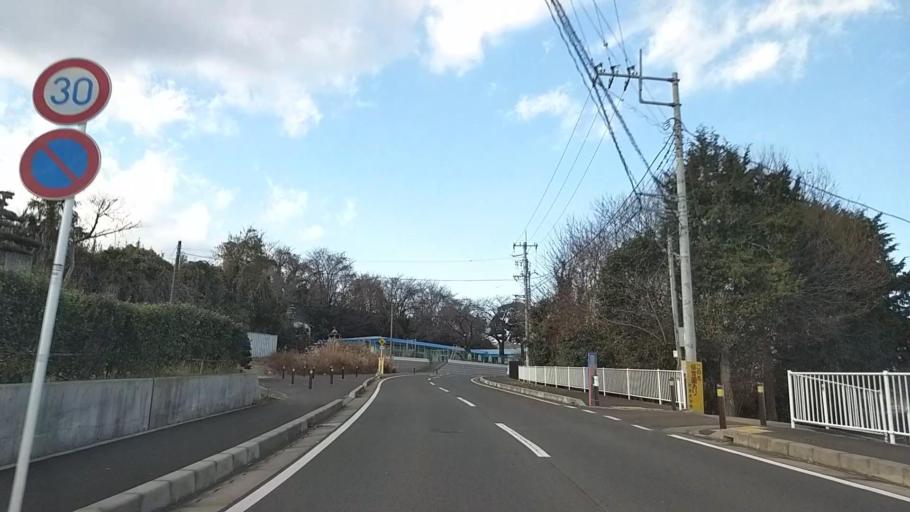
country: JP
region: Kanagawa
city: Isehara
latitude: 35.4106
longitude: 139.3180
